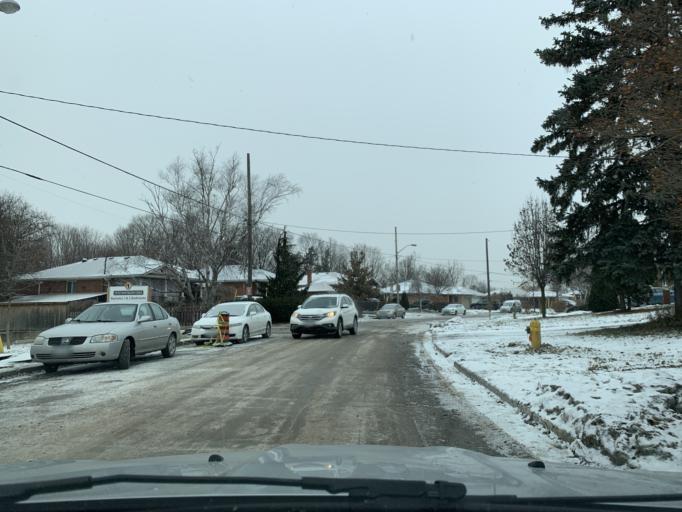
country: CA
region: Ontario
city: Concord
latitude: 43.7381
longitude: -79.4906
